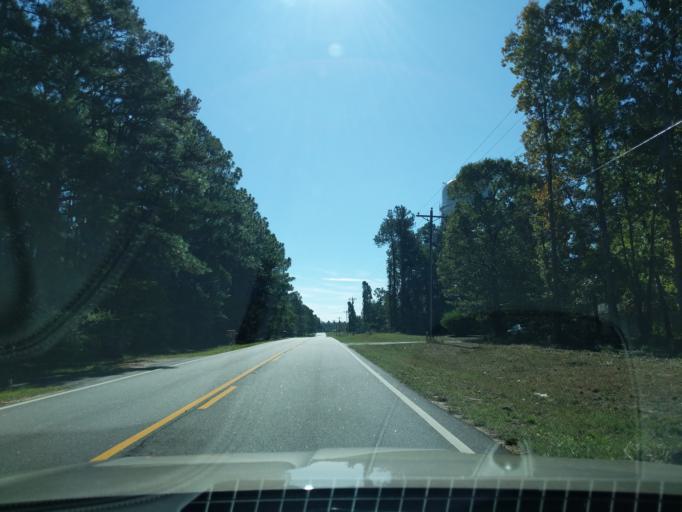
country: US
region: Georgia
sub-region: Richmond County
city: Hephzibah
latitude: 33.2742
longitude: -82.0139
